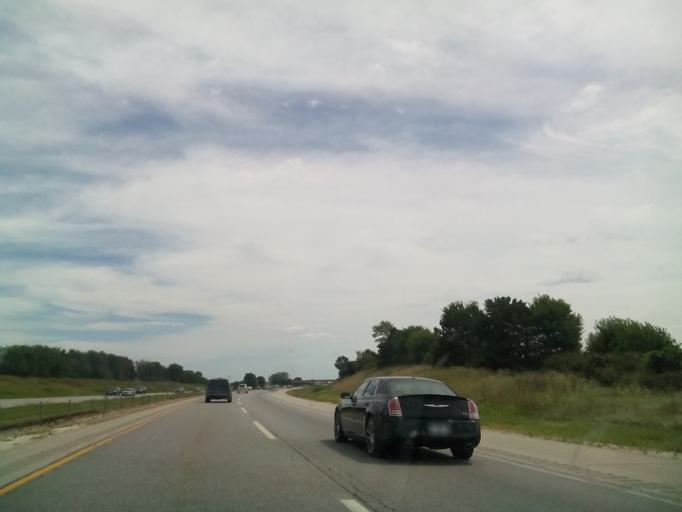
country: US
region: Illinois
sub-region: DeKalb County
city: Cortland
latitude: 41.8994
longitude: -88.6465
